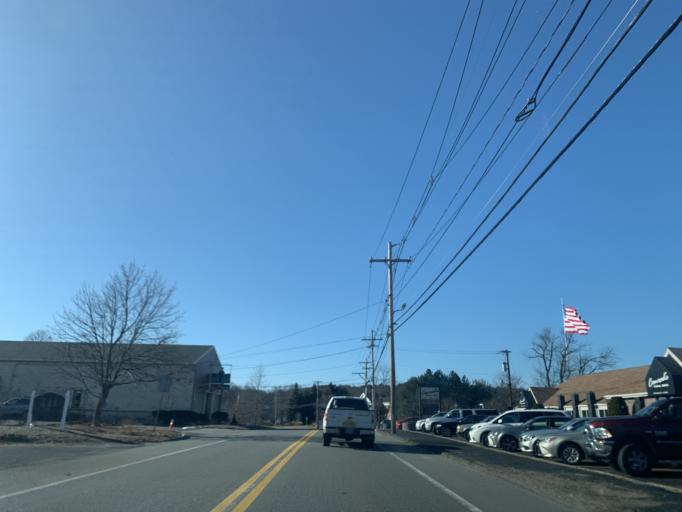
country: US
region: Massachusetts
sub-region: Middlesex County
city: Sudbury
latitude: 42.3632
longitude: -71.3940
